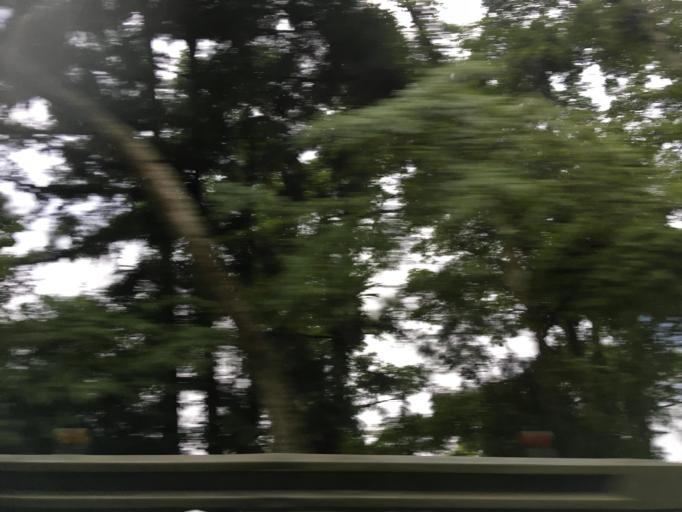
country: TW
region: Taiwan
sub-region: Yilan
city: Yilan
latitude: 24.5519
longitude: 121.5099
